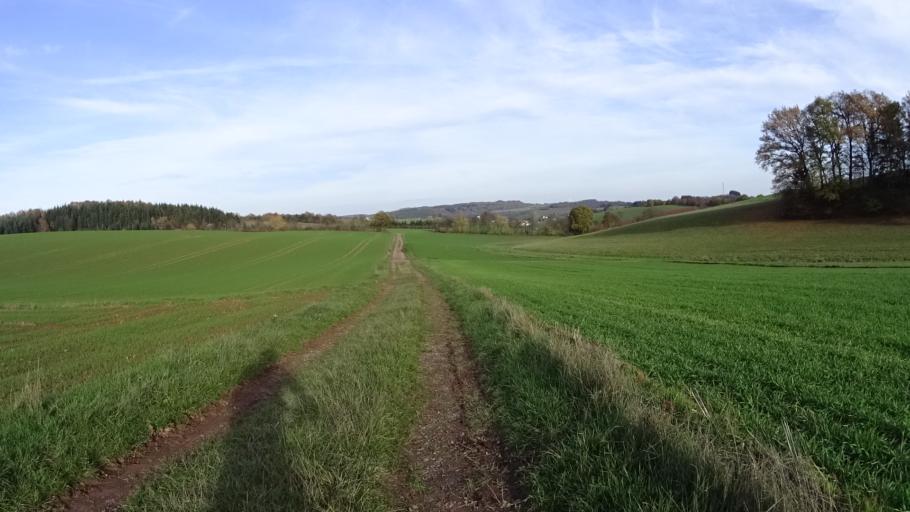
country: DE
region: Rheinland-Pfalz
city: Unterjeckenbach
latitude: 49.6831
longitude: 7.4846
